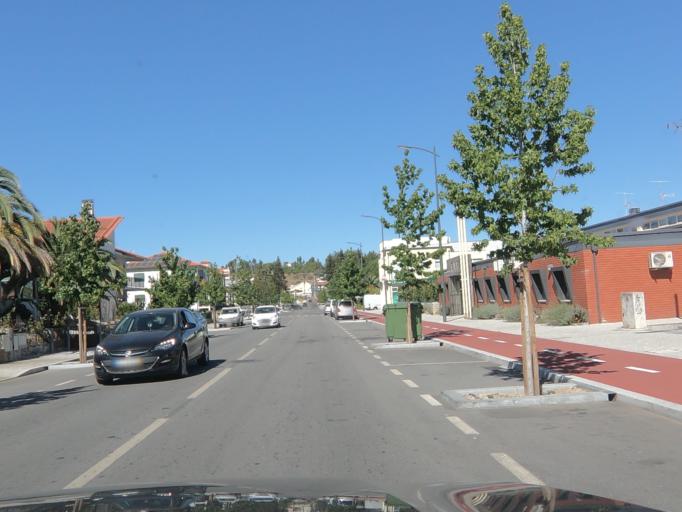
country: PT
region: Vila Real
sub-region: Valpacos
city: Valpacos
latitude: 41.6075
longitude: -7.3133
